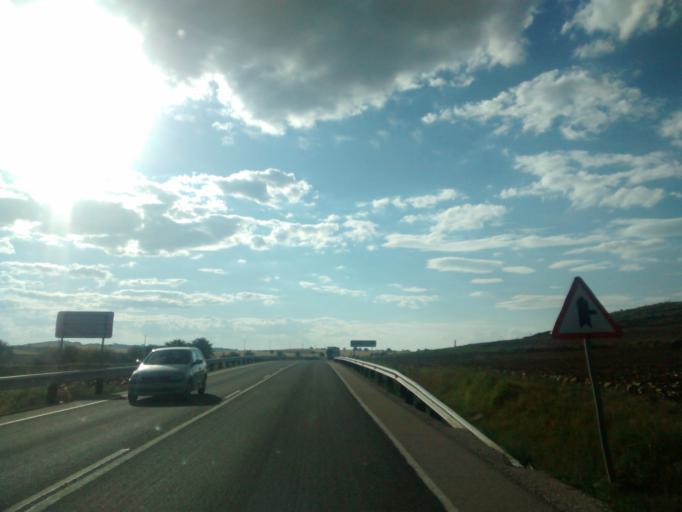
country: ES
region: Castille and Leon
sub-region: Provincia de Burgos
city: Basconcillos del Tozo
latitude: 42.6614
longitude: -3.9138
